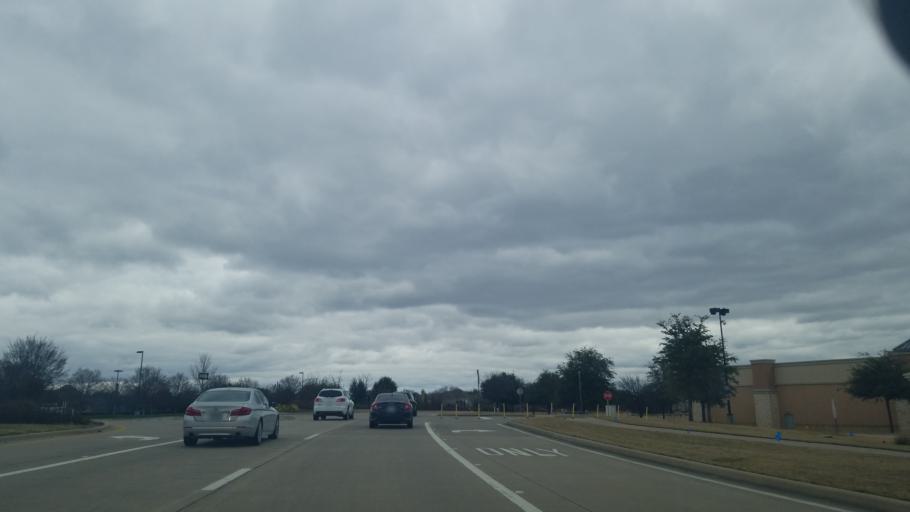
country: US
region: Texas
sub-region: Denton County
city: Copper Canyon
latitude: 33.0741
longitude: -97.0832
